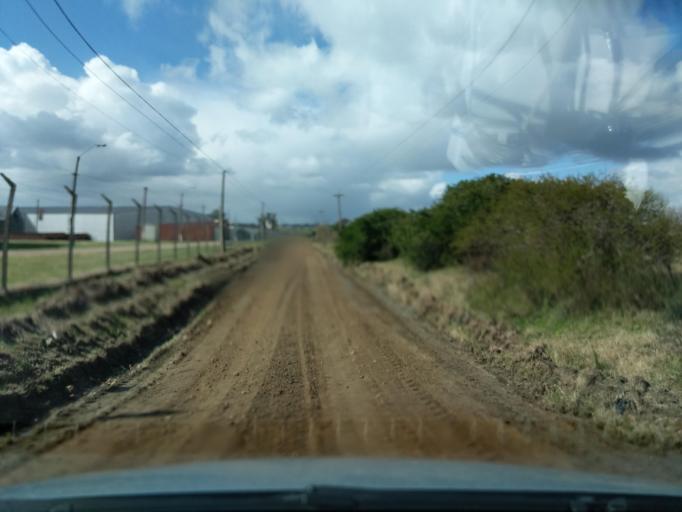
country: UY
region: Florida
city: Florida
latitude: -34.1138
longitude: -56.2323
